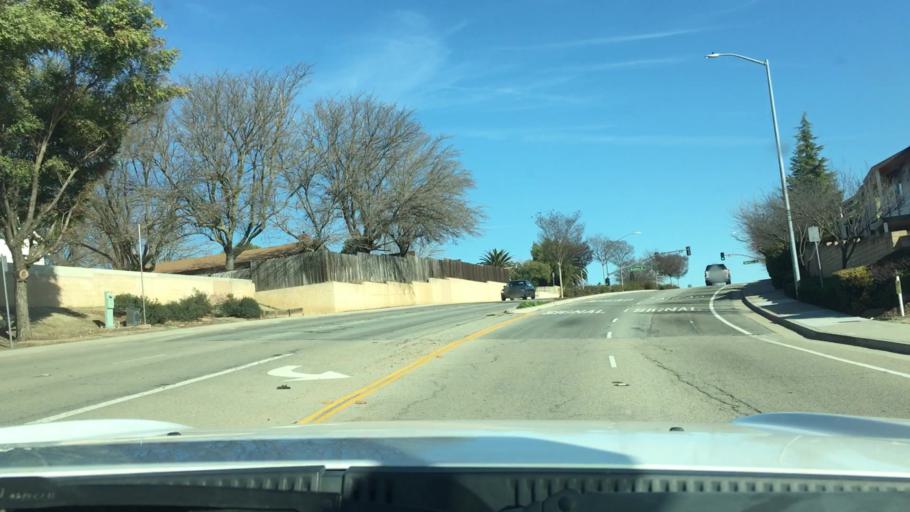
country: US
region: California
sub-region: San Luis Obispo County
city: Paso Robles
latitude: 35.6157
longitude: -120.6772
